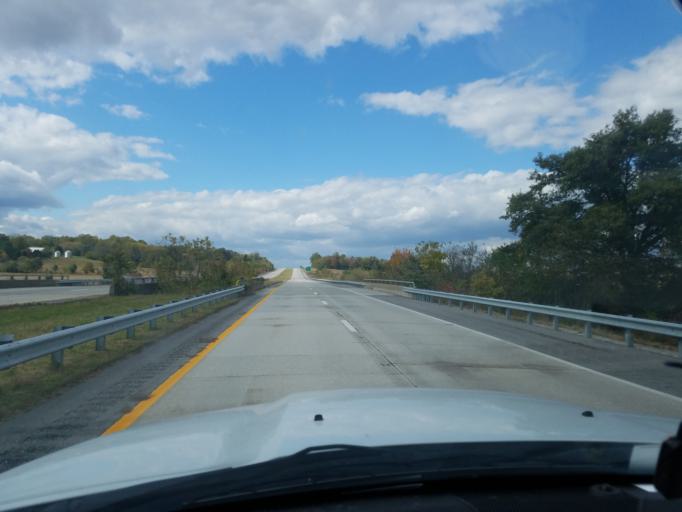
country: US
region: Kentucky
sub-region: Henderson County
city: Henderson
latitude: 37.7808
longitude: -87.4553
